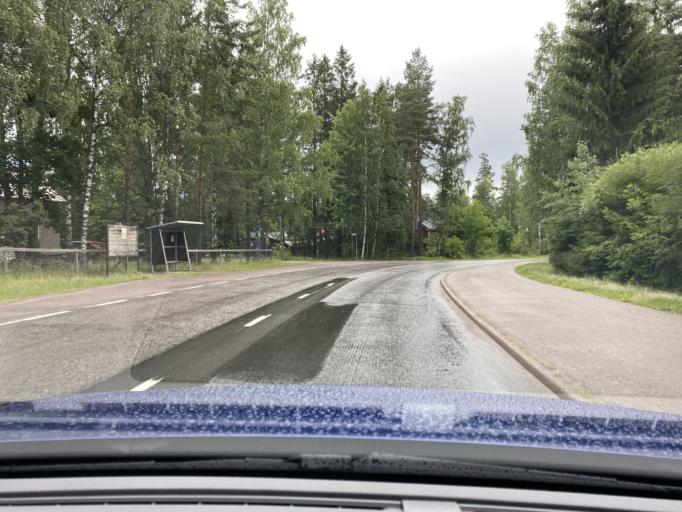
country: FI
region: Uusimaa
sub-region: Helsinki
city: Nurmijaervi
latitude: 60.5720
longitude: 24.7637
